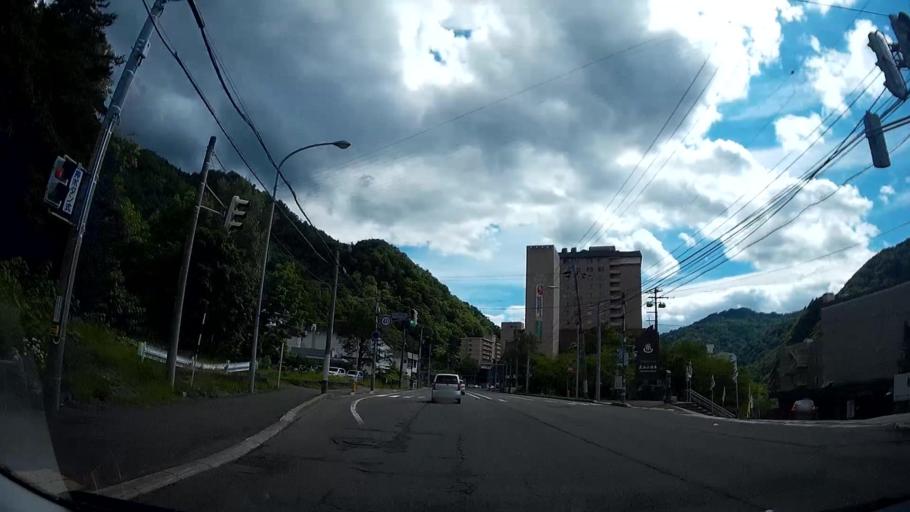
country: JP
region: Hokkaido
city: Sapporo
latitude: 42.9654
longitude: 141.1656
